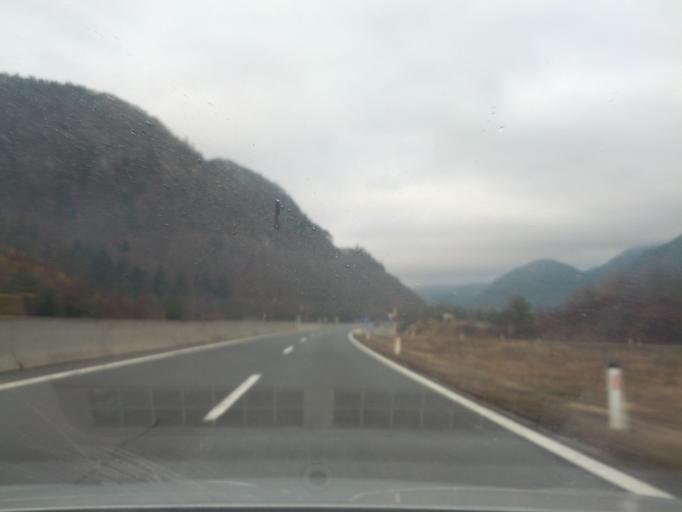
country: SI
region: Jesenice
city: Slovenski Javornik
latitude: 46.4151
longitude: 14.0946
